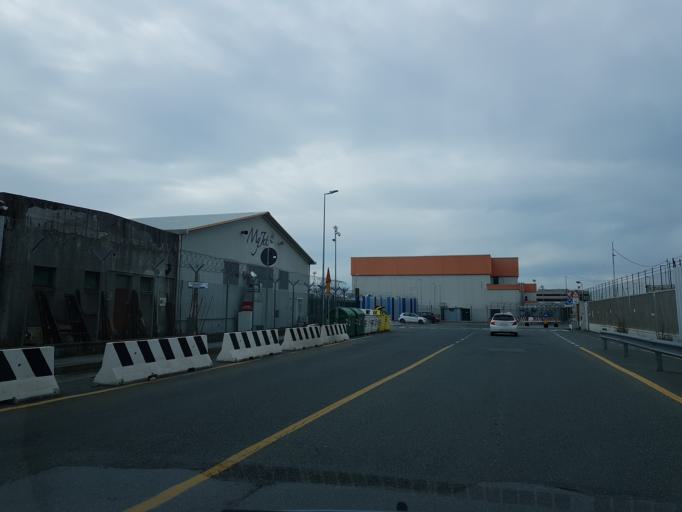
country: IT
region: Liguria
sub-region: Provincia di Genova
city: San Teodoro
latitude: 44.4194
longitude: 8.8532
